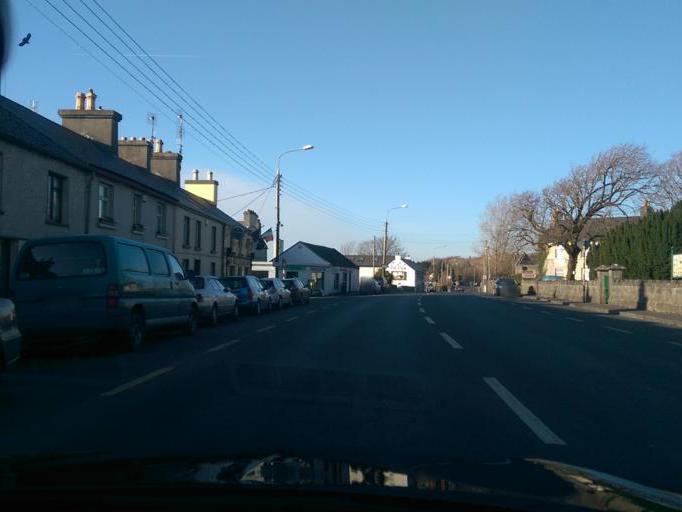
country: IE
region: Connaught
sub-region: County Galway
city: Oranmore
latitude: 53.2288
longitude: -8.8807
